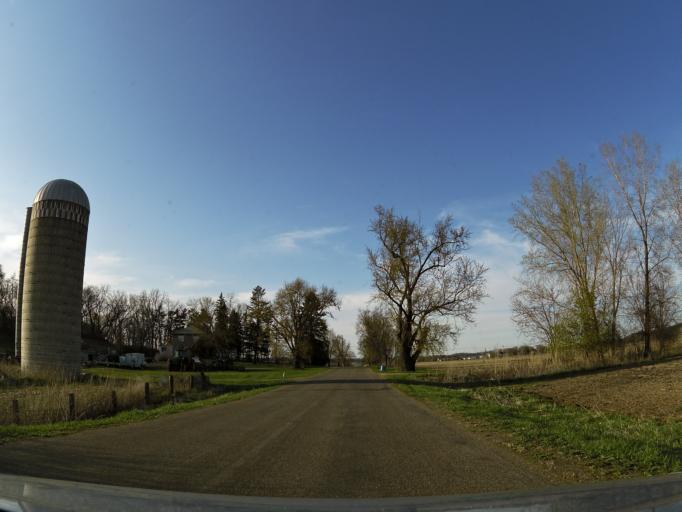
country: US
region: Minnesota
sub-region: Washington County
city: Afton
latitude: 44.8515
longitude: -92.7158
